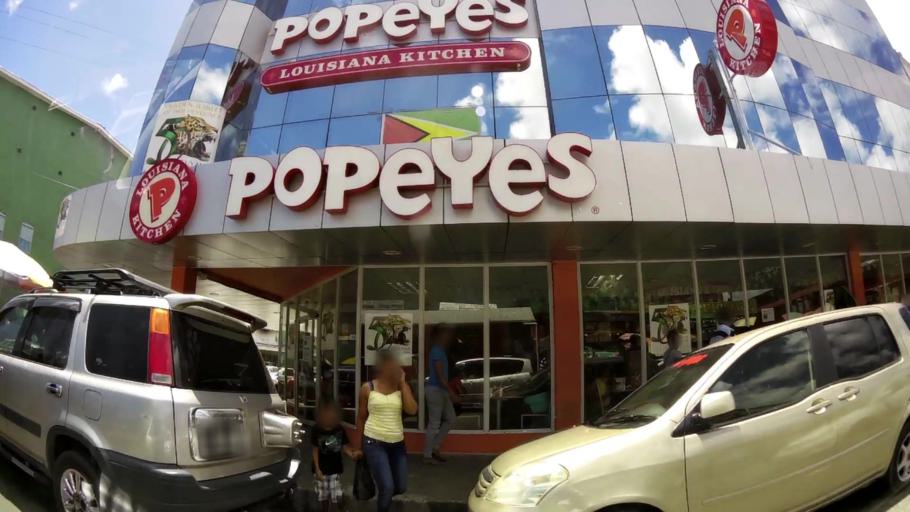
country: GY
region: Demerara-Mahaica
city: Georgetown
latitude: 6.8107
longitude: -58.1674
